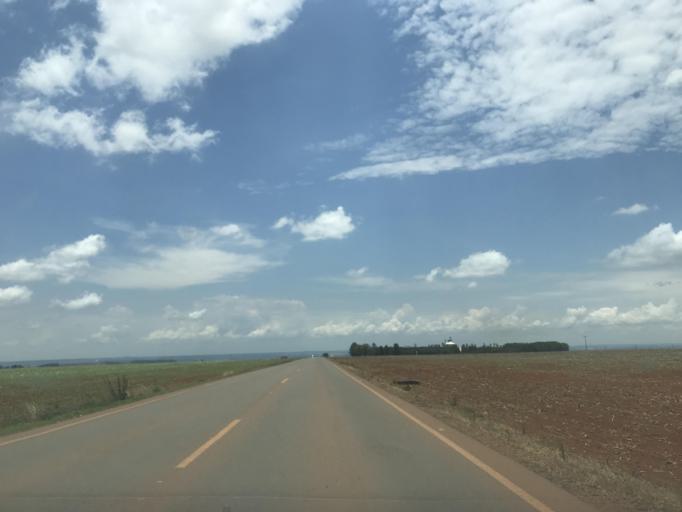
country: BR
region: Goias
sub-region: Vianopolis
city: Vianopolis
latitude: -16.5393
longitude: -48.2564
